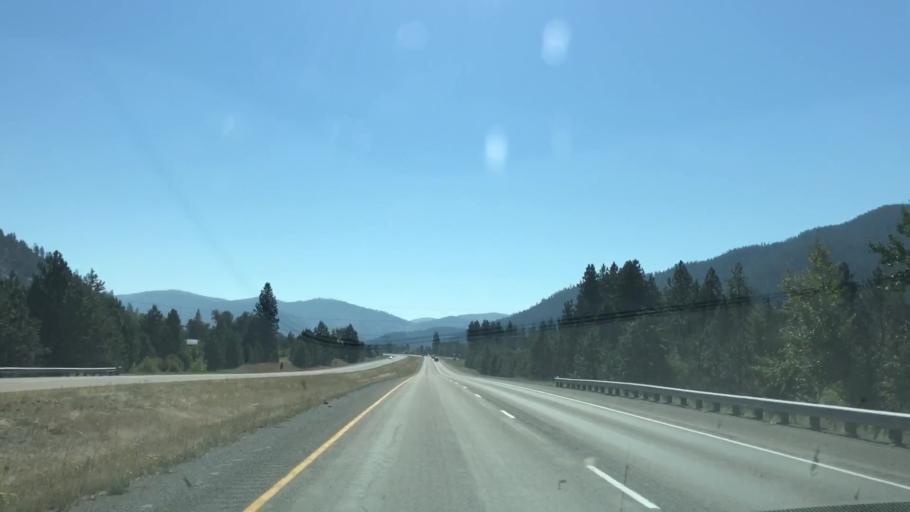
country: US
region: Montana
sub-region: Missoula County
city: Clinton
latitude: 46.8054
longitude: -113.7780
